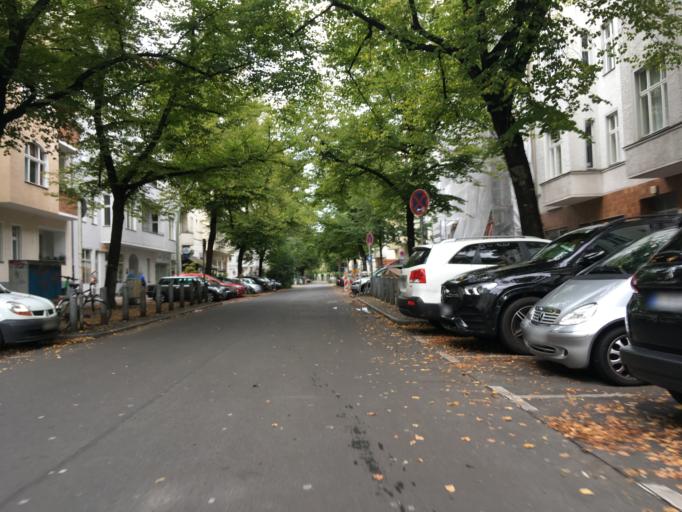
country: DE
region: Berlin
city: Halensee
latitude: 52.5009
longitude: 13.3005
